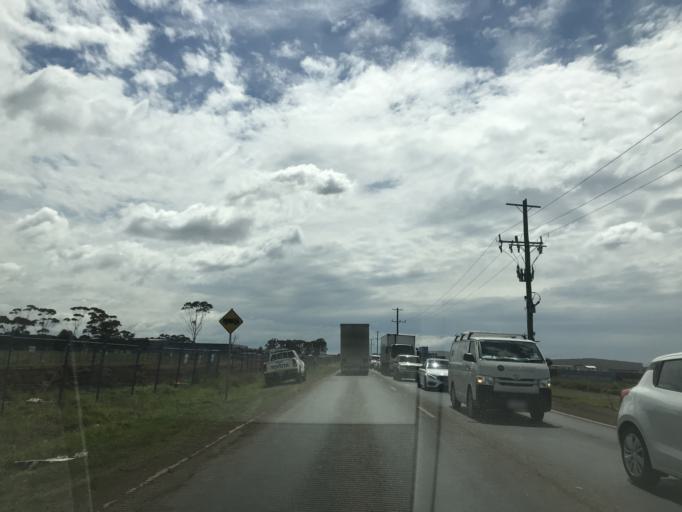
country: AU
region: Victoria
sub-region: Wyndham
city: Truganina
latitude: -37.8235
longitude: 144.7493
